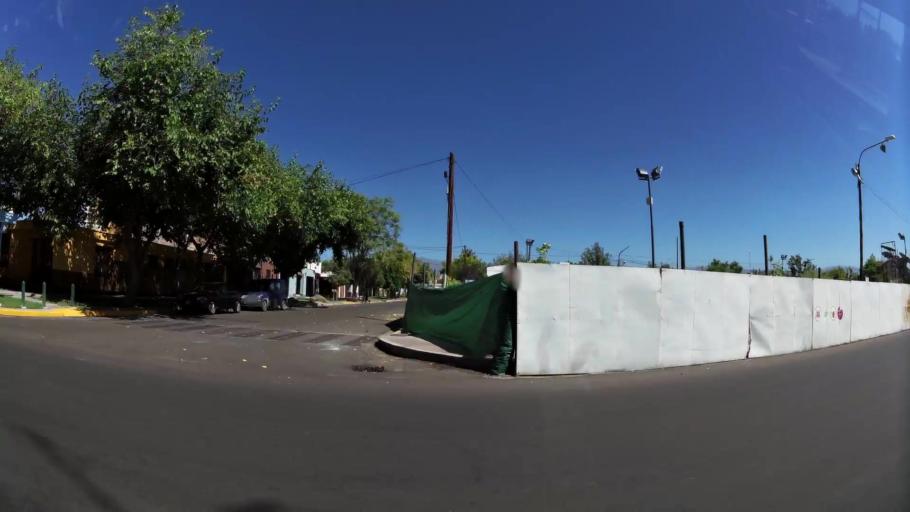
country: AR
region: Mendoza
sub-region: Departamento de Godoy Cruz
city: Godoy Cruz
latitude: -32.9507
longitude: -68.8562
